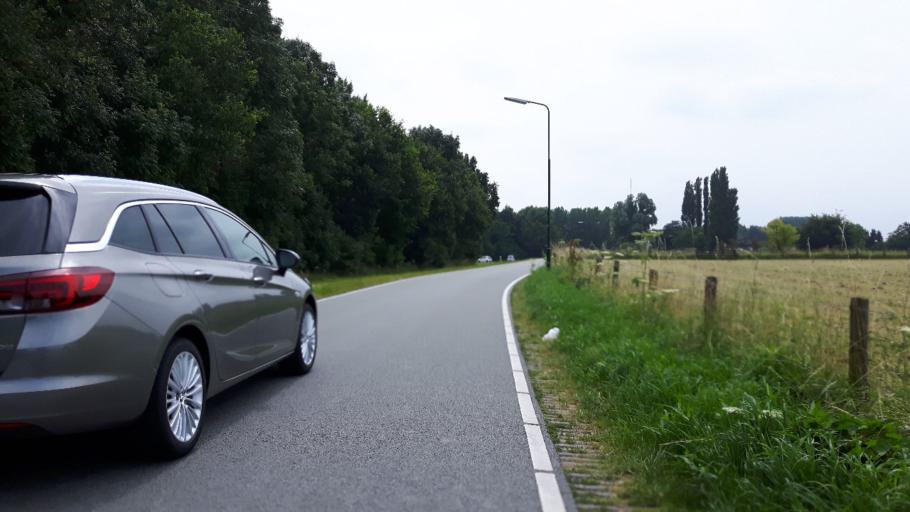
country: NL
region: Utrecht
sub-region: Gemeente IJsselstein
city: IJsselstein
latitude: 52.0413
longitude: 5.0347
